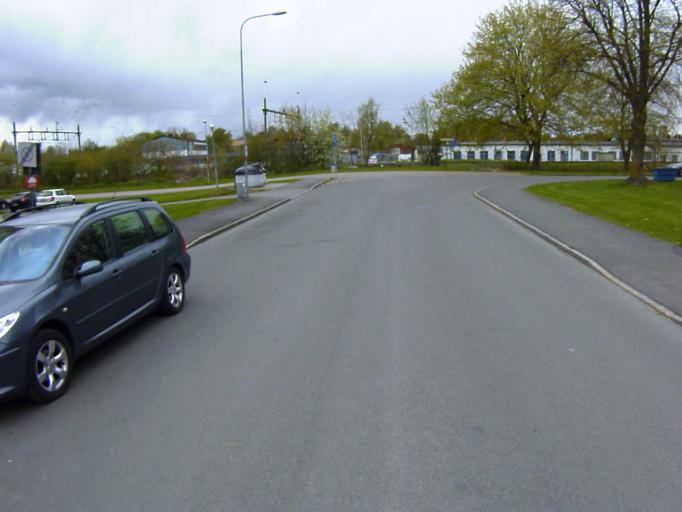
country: SE
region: Skane
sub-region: Kristianstads Kommun
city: Kristianstad
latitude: 56.0436
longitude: 14.1619
